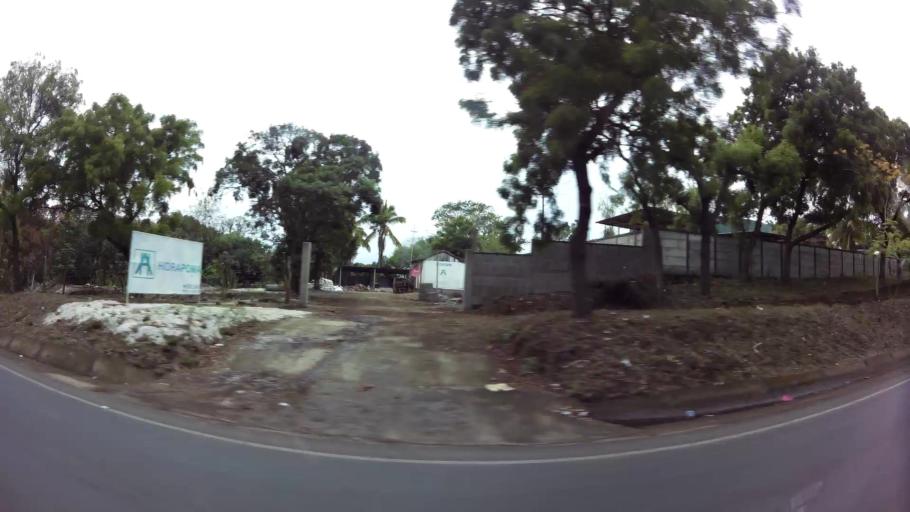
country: NI
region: Masaya
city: Masaya
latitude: 11.9633
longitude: -86.0824
